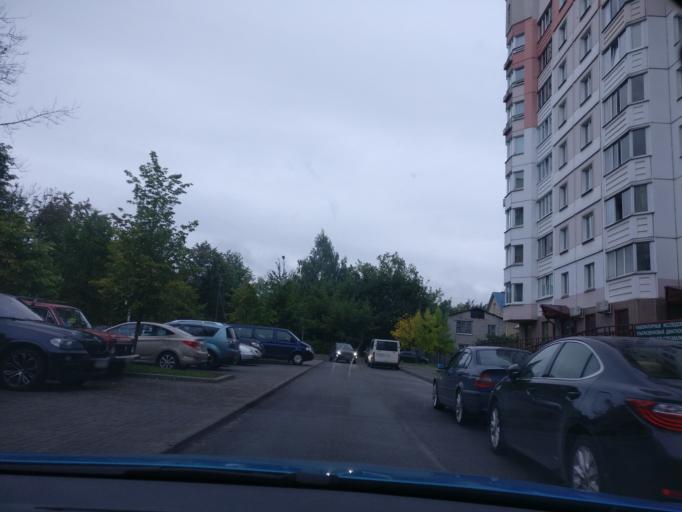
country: BY
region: Minsk
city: Minsk
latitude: 53.9307
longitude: 27.5484
